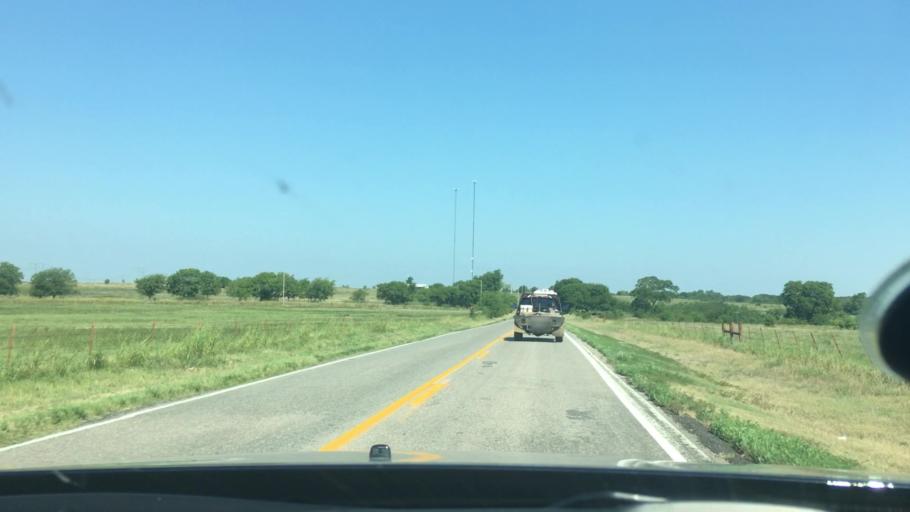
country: US
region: Oklahoma
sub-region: Johnston County
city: Tishomingo
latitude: 34.1885
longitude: -96.5285
